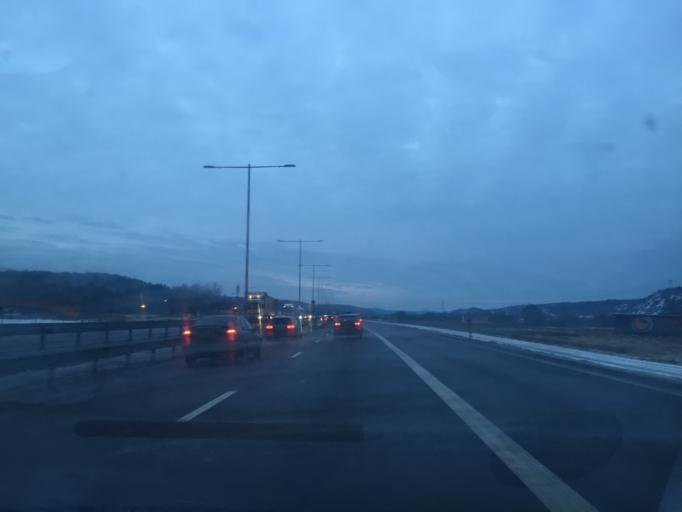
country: SE
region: Vaestra Goetaland
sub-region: Goteborg
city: Gardsten
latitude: 57.8035
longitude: 12.0078
